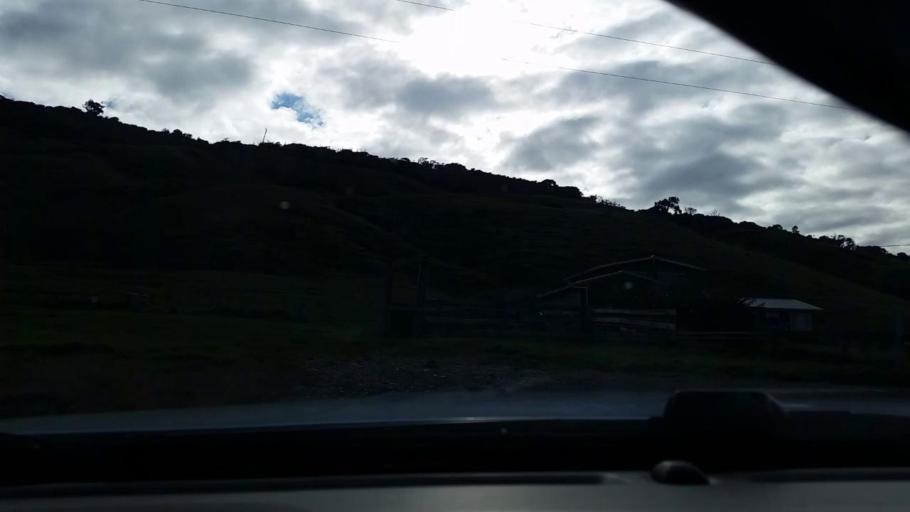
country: NZ
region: Southland
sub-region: Southland District
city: Riverton
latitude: -46.3305
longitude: 167.7125
